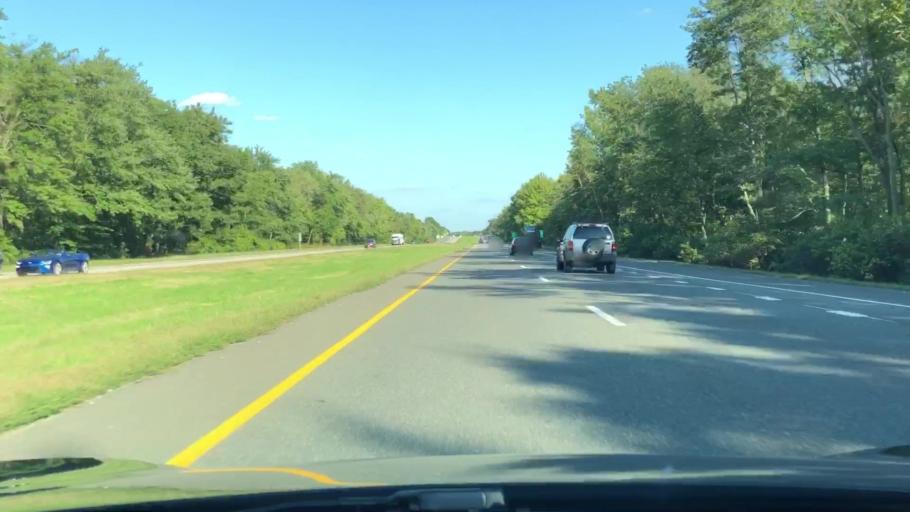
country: US
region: Pennsylvania
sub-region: Delaware County
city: Chester
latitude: 39.8029
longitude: -75.3353
